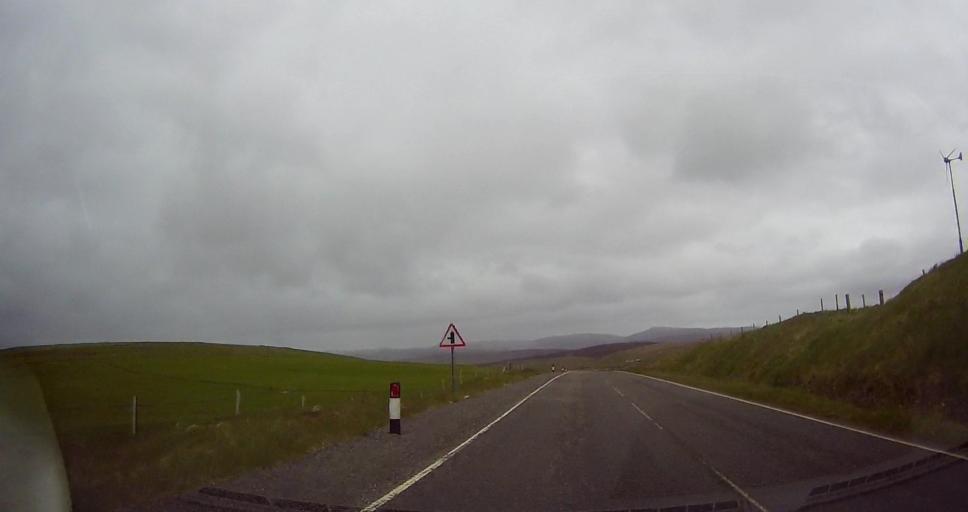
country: GB
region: Scotland
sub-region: Shetland Islands
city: Lerwick
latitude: 60.2621
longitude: -1.4034
